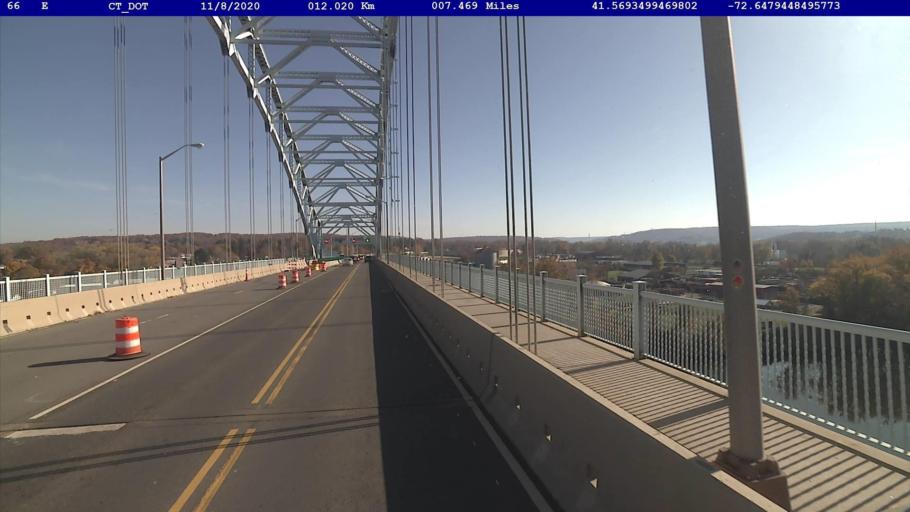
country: US
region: Connecticut
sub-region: Middlesex County
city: Portland
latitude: 41.5701
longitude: -72.6475
